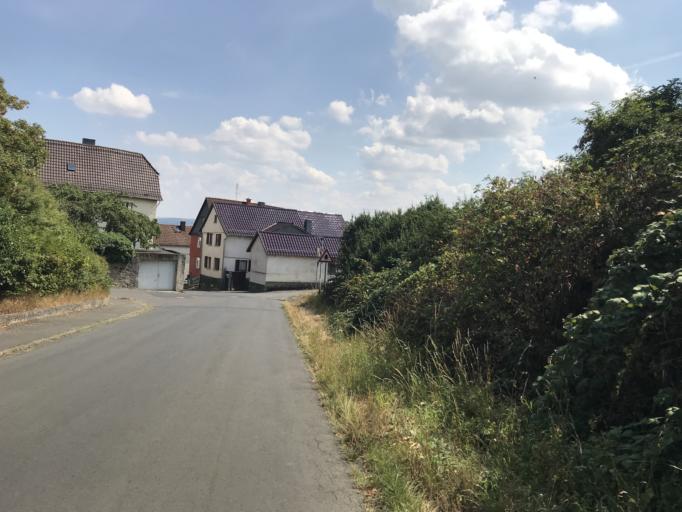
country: DE
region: Hesse
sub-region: Regierungsbezirk Darmstadt
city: Wolfersheim
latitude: 50.4402
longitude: 8.8290
